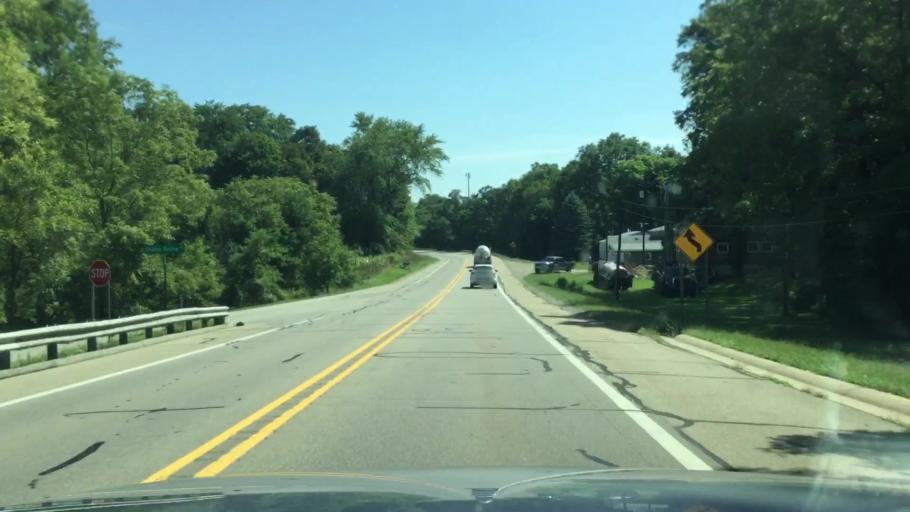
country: US
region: Michigan
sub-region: Washtenaw County
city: Manchester
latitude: 42.0725
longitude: -84.0819
